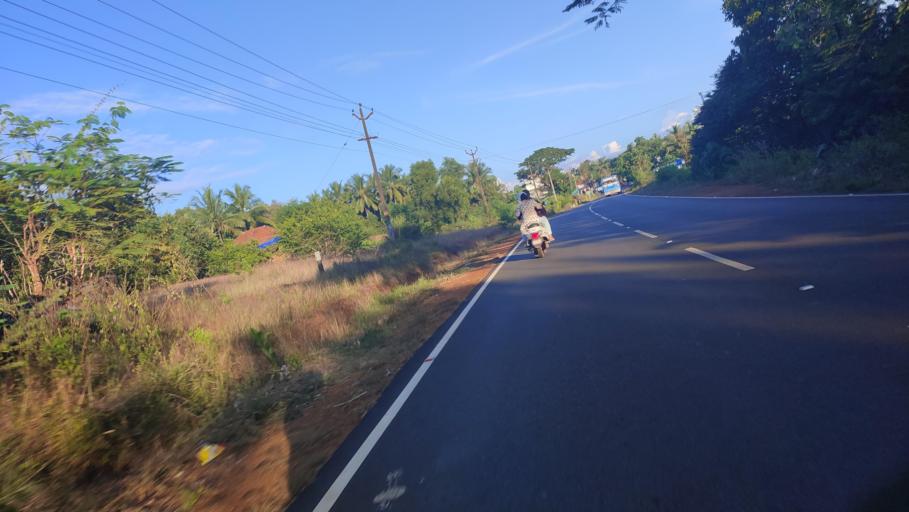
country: IN
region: Kerala
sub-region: Kasaragod District
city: Kasaragod
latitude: 12.4578
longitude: 75.0940
